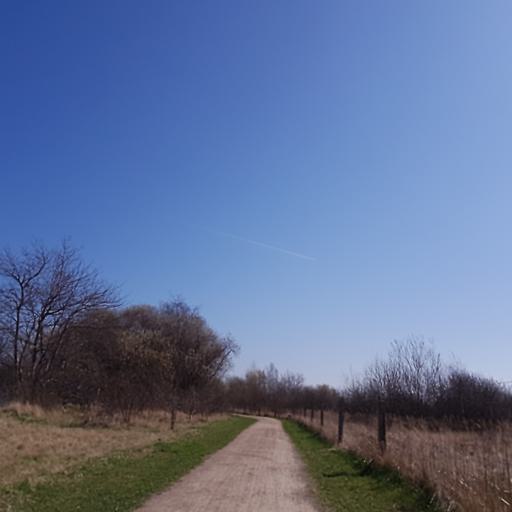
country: DK
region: Capital Region
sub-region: Frederiksberg Kommune
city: Frederiksberg
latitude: 55.6366
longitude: 12.5373
